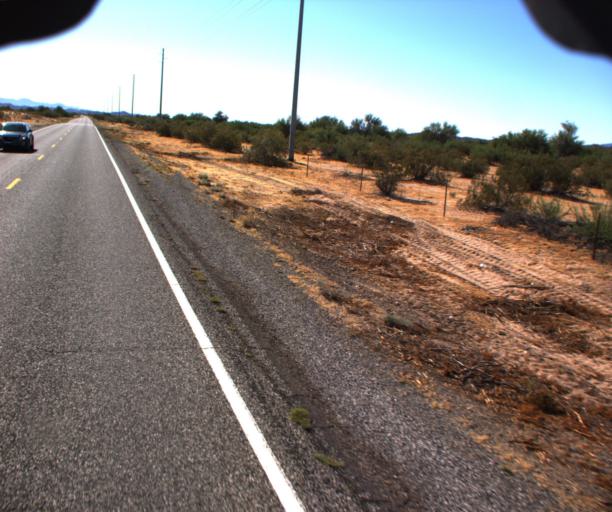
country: US
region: Arizona
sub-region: La Paz County
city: Cienega Springs
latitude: 33.9893
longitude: -114.0763
